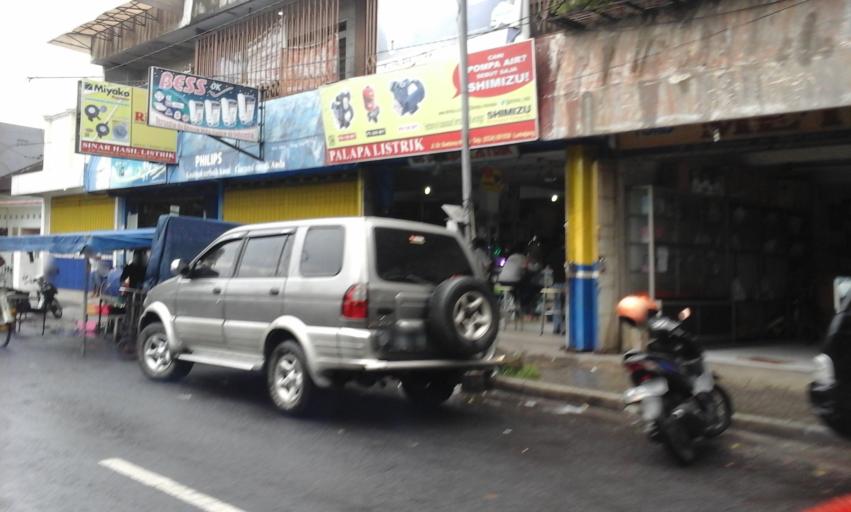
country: ID
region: East Java
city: Lumajang
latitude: -8.1301
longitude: 113.2226
